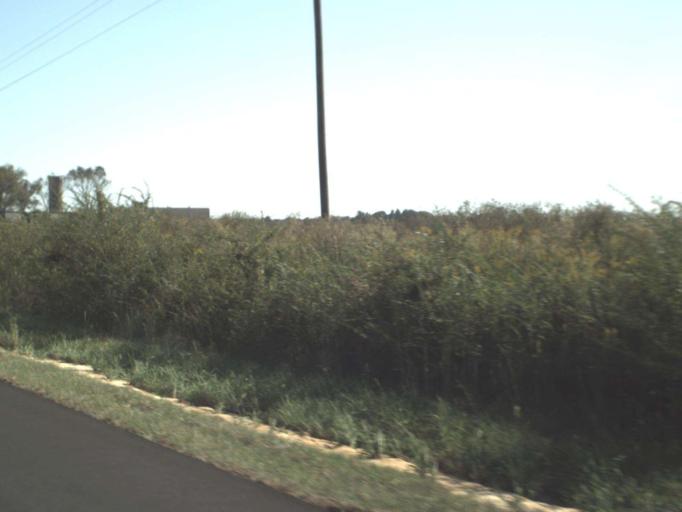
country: US
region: Alabama
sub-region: Covington County
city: Florala
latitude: 30.8785
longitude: -86.2669
